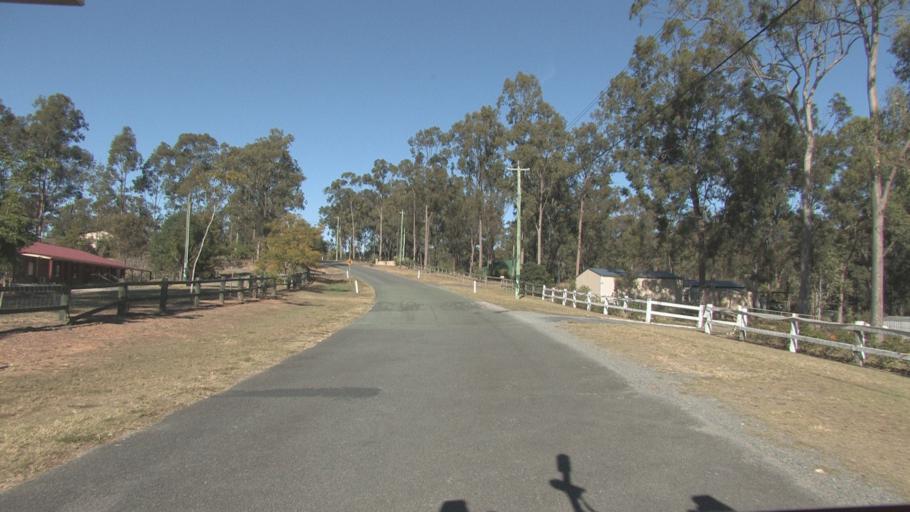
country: AU
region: Queensland
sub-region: Ipswich
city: Springfield Lakes
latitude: -27.6988
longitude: 152.9303
